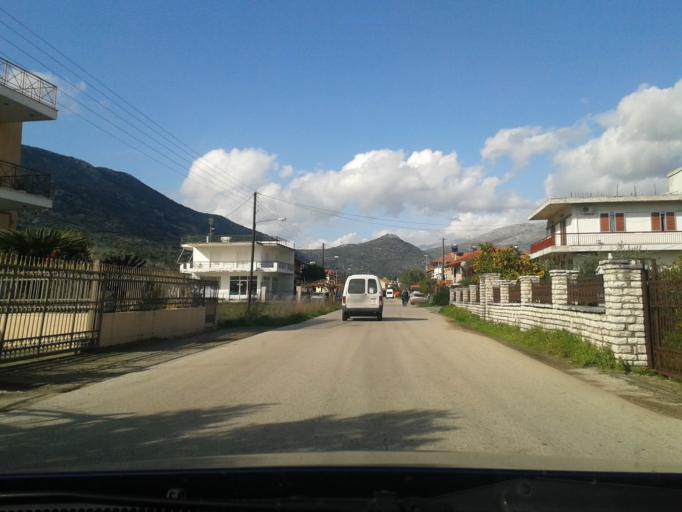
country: GR
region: West Greece
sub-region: Nomos Aitolias kai Akarnanias
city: Astakos
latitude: 38.5755
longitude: 21.0922
